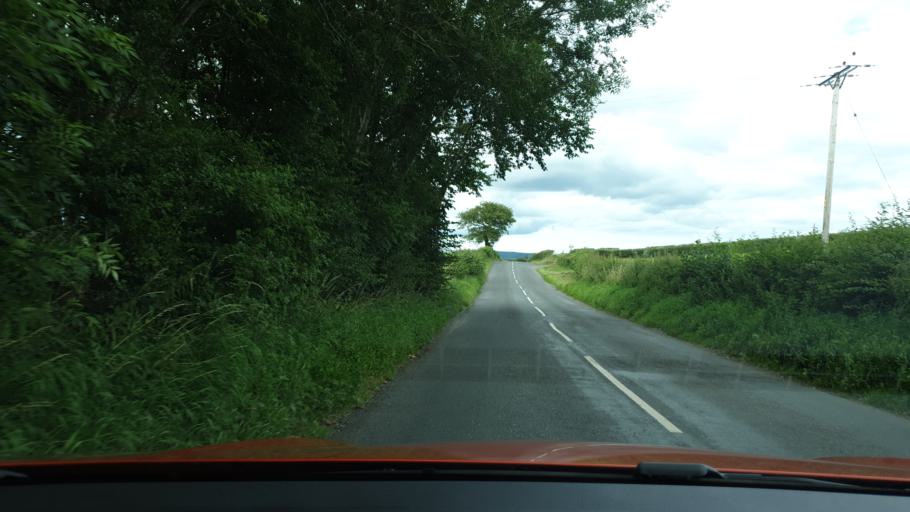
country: GB
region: England
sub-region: Cumbria
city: Penrith
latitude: 54.6225
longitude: -2.7981
